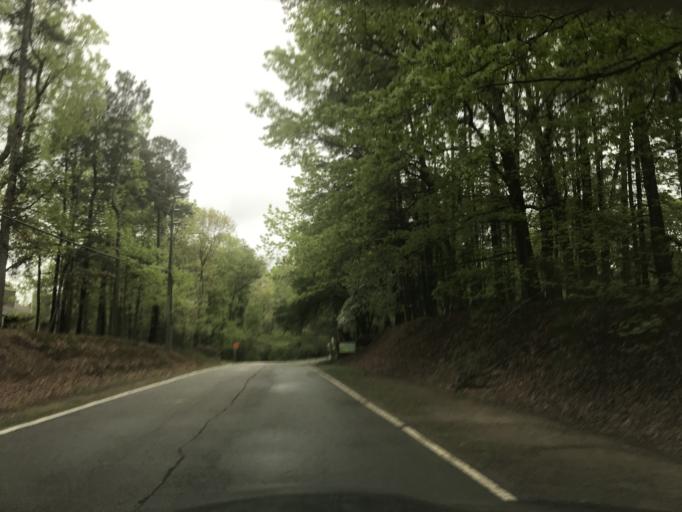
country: US
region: North Carolina
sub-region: Wake County
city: West Raleigh
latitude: 35.7561
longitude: -78.7049
